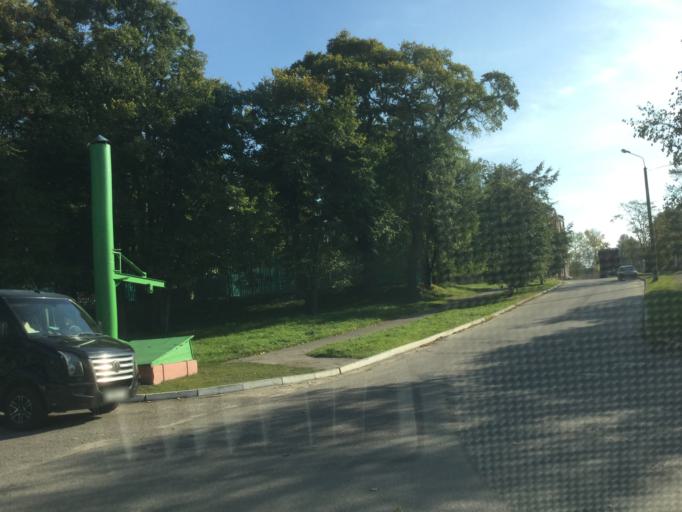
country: BY
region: Vitebsk
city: Vitebsk
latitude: 55.1742
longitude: 30.1957
